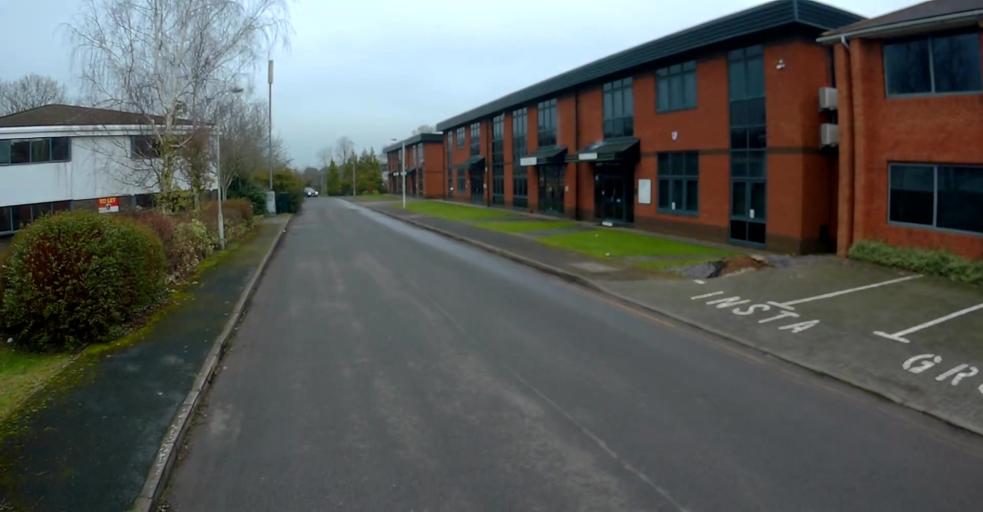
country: GB
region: England
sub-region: Hampshire
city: Eversley
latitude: 51.3752
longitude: -0.8917
